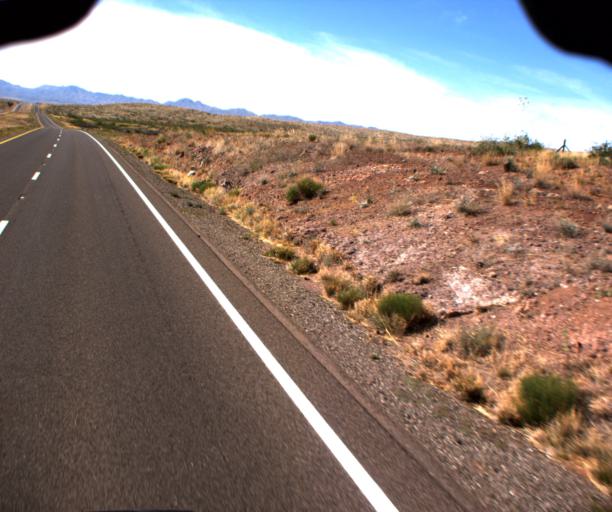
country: US
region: Arizona
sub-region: Cochise County
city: Willcox
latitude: 32.4413
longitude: -109.6640
